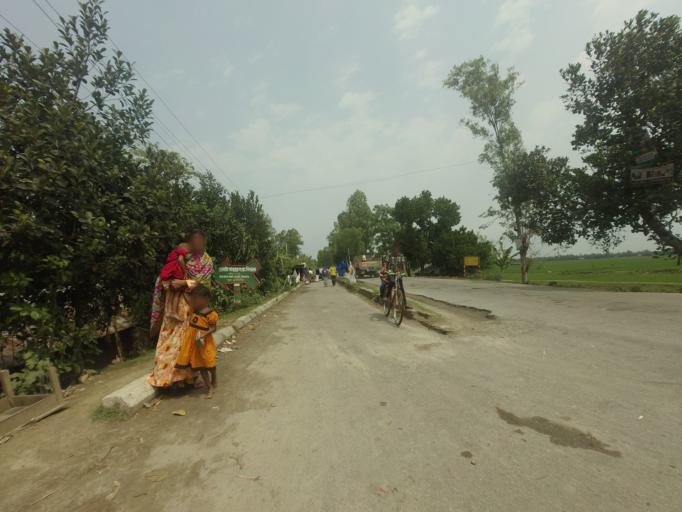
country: BD
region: Rajshahi
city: Sirajganj
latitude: 24.3274
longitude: 89.6991
